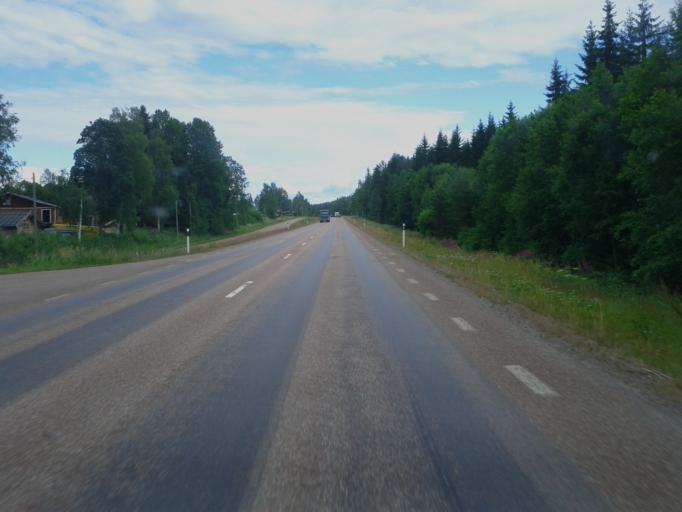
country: SE
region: Dalarna
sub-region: Faluns Kommun
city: Bjursas
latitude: 60.7424
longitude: 15.3996
